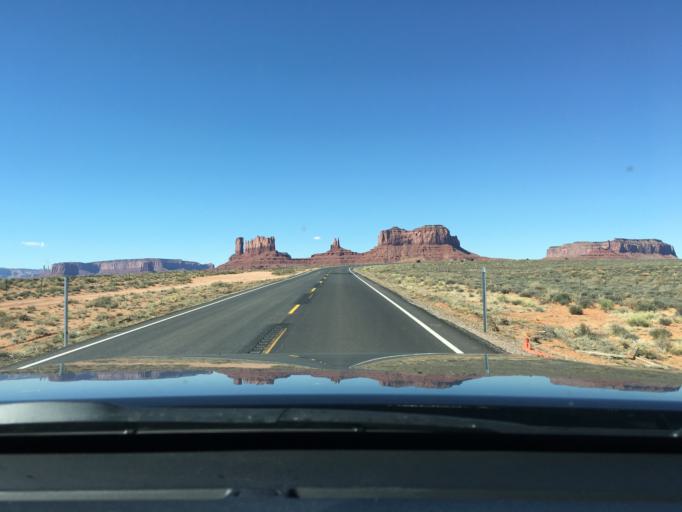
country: US
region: Arizona
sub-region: Navajo County
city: Kayenta
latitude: 37.0702
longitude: -110.0347
